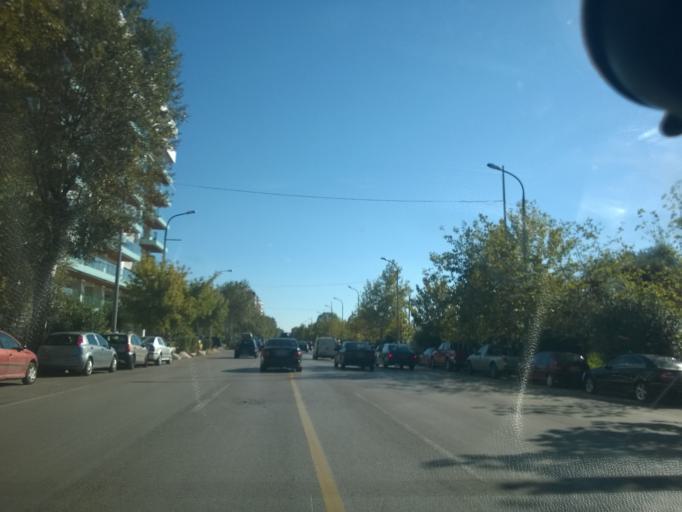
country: GR
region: Central Macedonia
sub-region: Nomos Thessalonikis
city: Triandria
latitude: 40.6137
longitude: 22.9524
